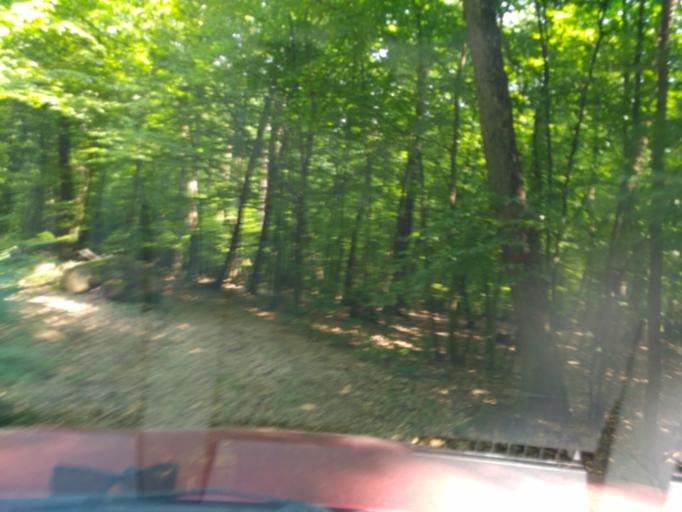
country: SK
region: Kosicky
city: Moldava nad Bodvou
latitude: 48.6374
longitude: 21.0405
